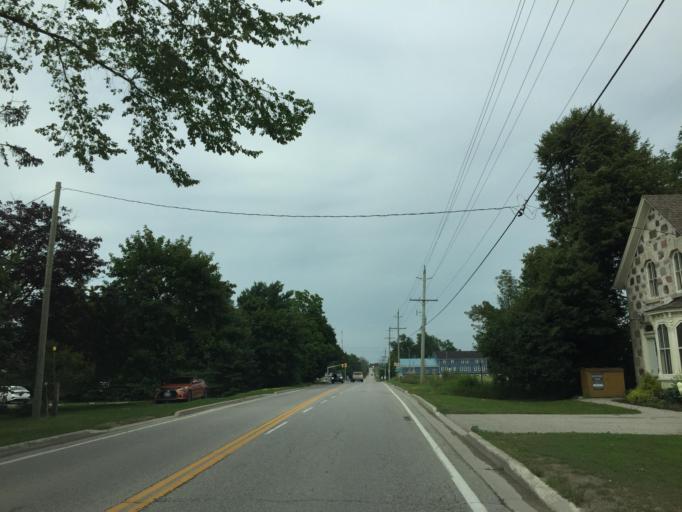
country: CA
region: Ontario
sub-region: Wellington County
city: Guelph
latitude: 43.5846
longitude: -80.3010
